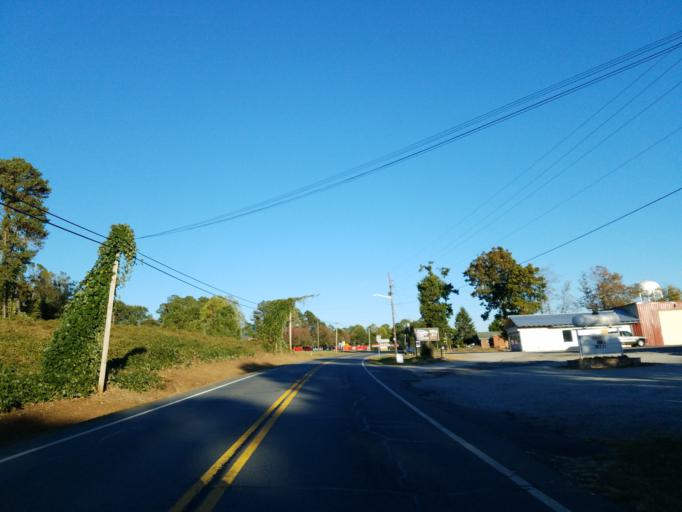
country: US
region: Georgia
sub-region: Dawson County
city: Dawsonville
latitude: 34.4219
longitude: -84.1258
